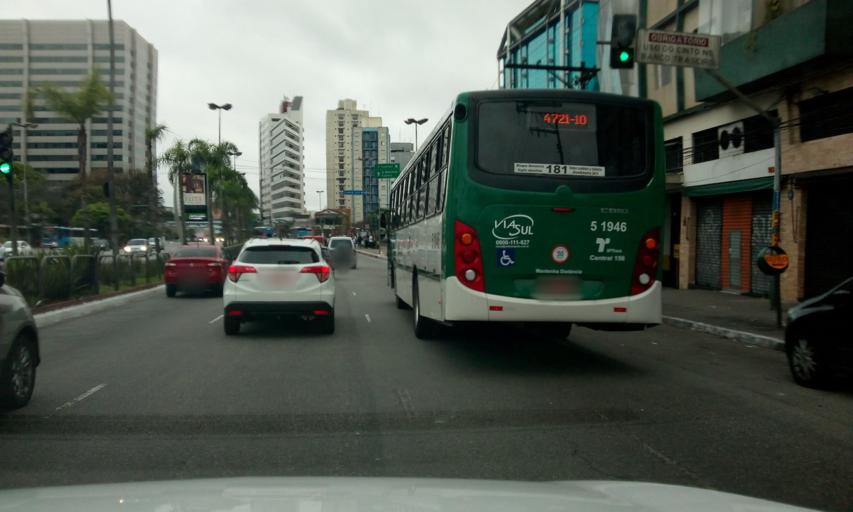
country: BR
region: Sao Paulo
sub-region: Diadema
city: Diadema
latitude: -23.6364
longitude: -46.6412
